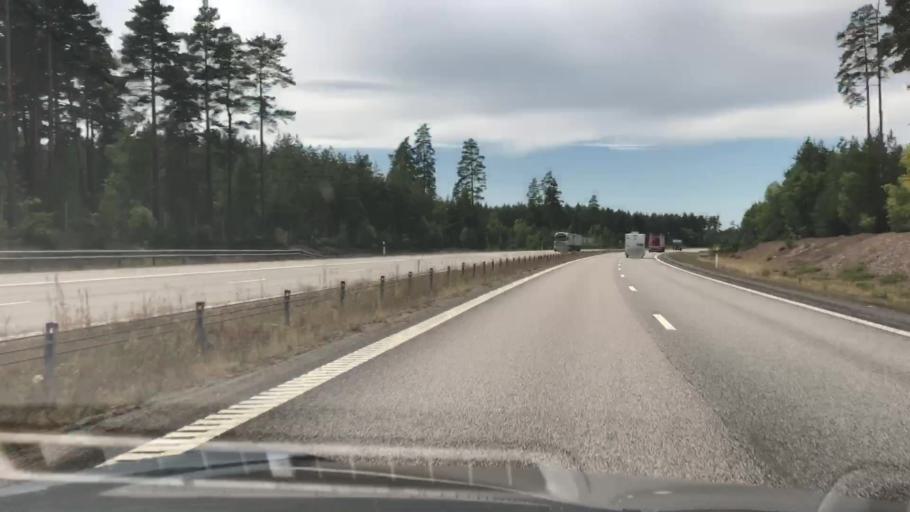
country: SE
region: Skane
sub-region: Bromolla Kommun
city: Bromoella
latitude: 56.0466
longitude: 14.4337
